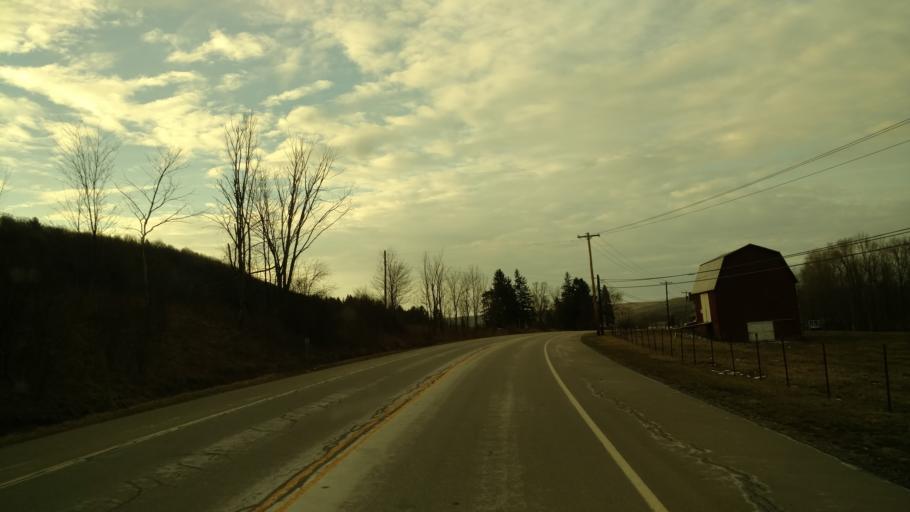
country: US
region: New York
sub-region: Allegany County
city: Wellsville
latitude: 42.0699
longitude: -77.9188
